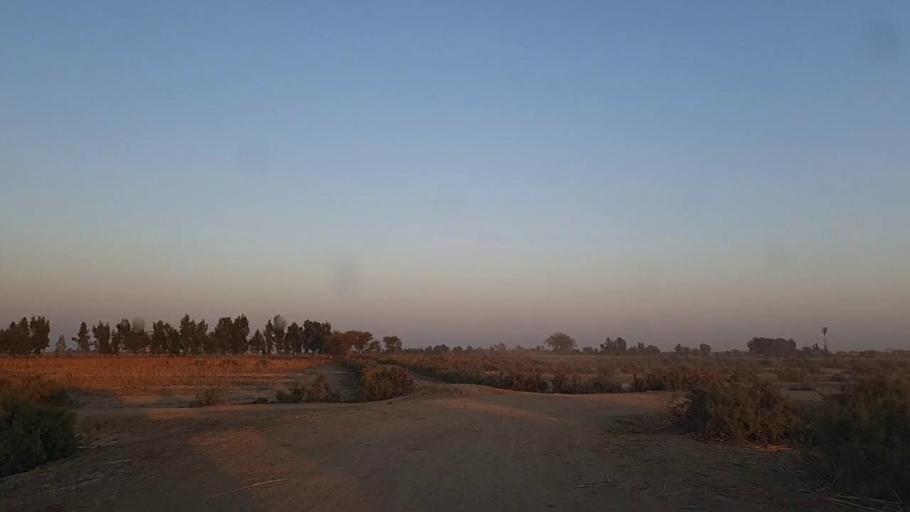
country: PK
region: Sindh
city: Samaro
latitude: 25.3181
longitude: 69.3689
